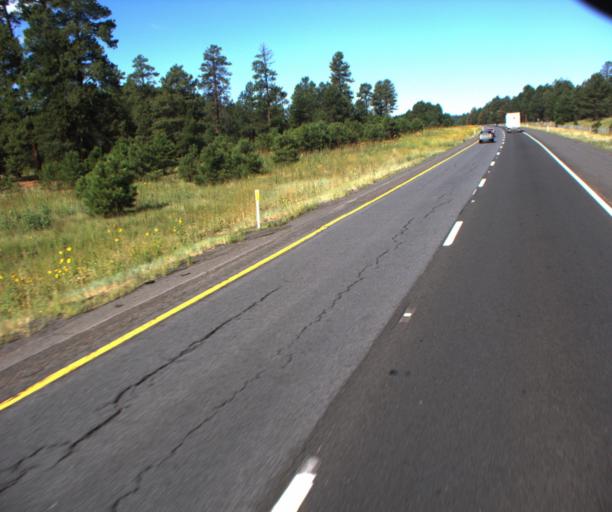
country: US
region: Arizona
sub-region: Coconino County
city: Parks
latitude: 35.2496
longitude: -111.8667
